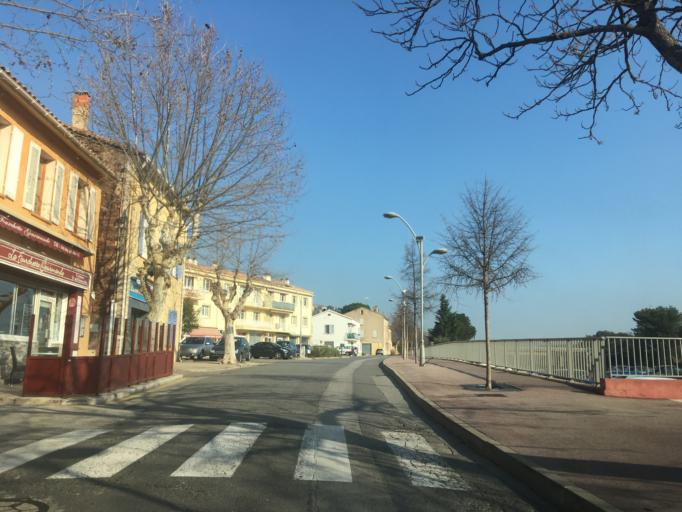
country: FR
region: Provence-Alpes-Cote d'Azur
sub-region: Departement du Var
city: Le Cannet-des-Maures
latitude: 43.3904
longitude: 6.3426
